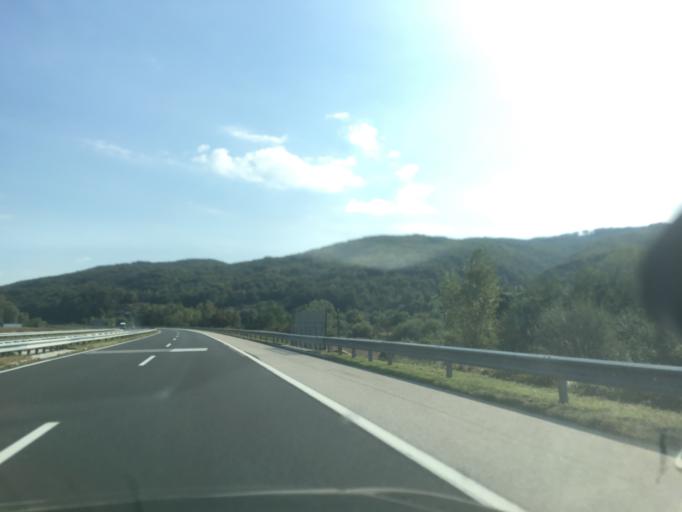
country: SI
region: Brezice
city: Brezice
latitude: 45.8831
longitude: 15.6208
